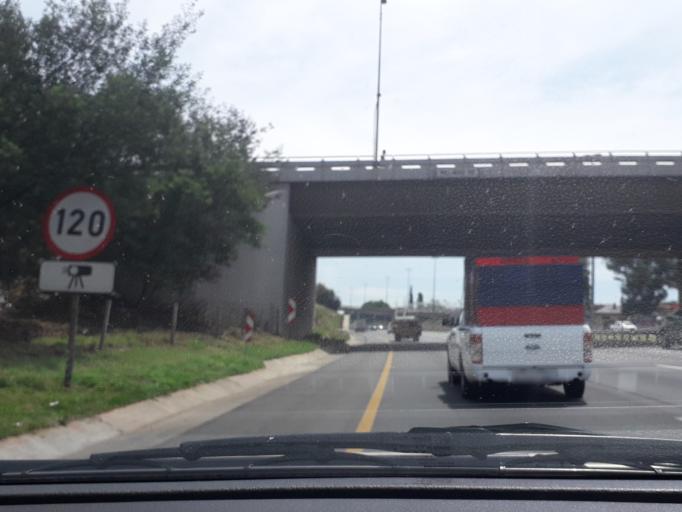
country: ZA
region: Gauteng
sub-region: City of Johannesburg Metropolitan Municipality
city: Roodepoort
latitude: -26.1791
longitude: 27.9453
